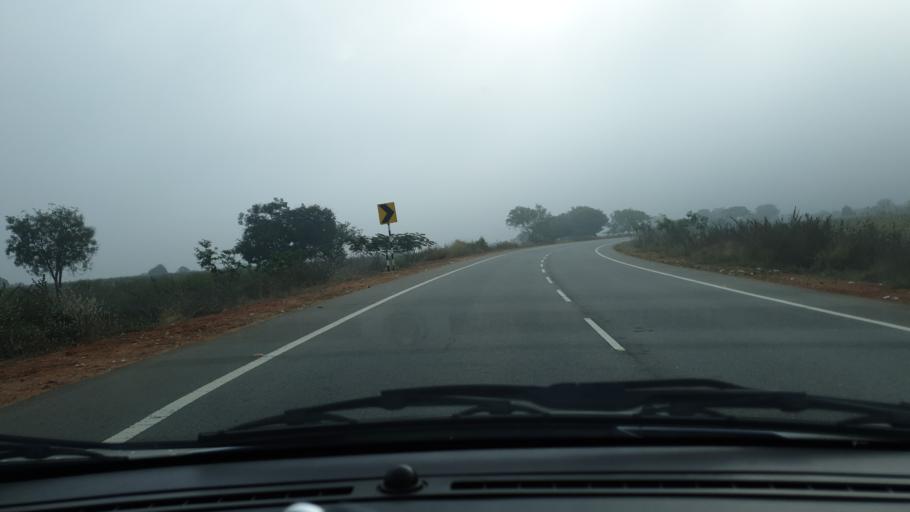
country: IN
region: Telangana
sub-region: Nalgonda
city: Devarkonda
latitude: 16.6400
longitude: 78.6308
